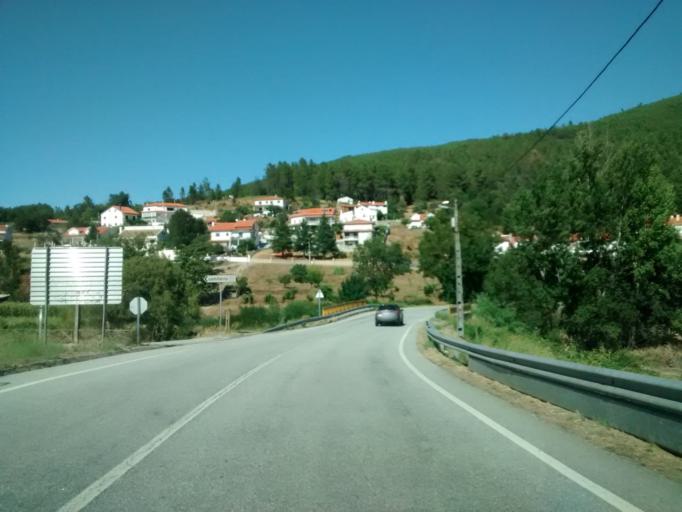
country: PT
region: Castelo Branco
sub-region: Belmonte
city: Belmonte
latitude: 40.4055
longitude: -7.3996
